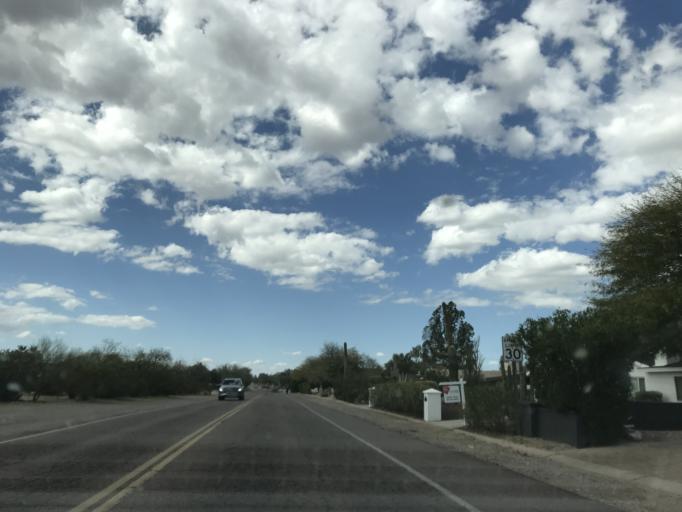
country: US
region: Arizona
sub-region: Maricopa County
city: Paradise Valley
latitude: 33.5171
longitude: -111.9918
